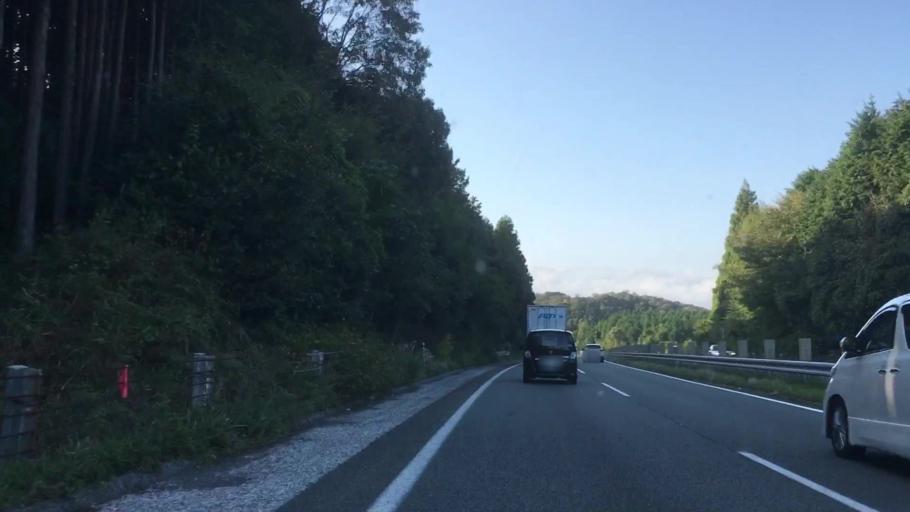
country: JP
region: Yamaguchi
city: Ogori-shimogo
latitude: 34.1568
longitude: 131.3328
